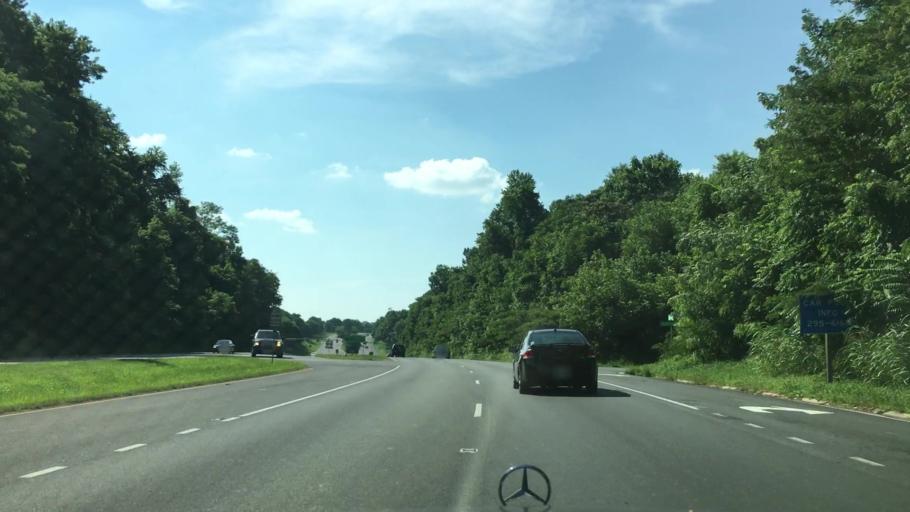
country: US
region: Virginia
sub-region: City of Charlottesville
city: Charlottesville
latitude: 38.0220
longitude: -78.4315
